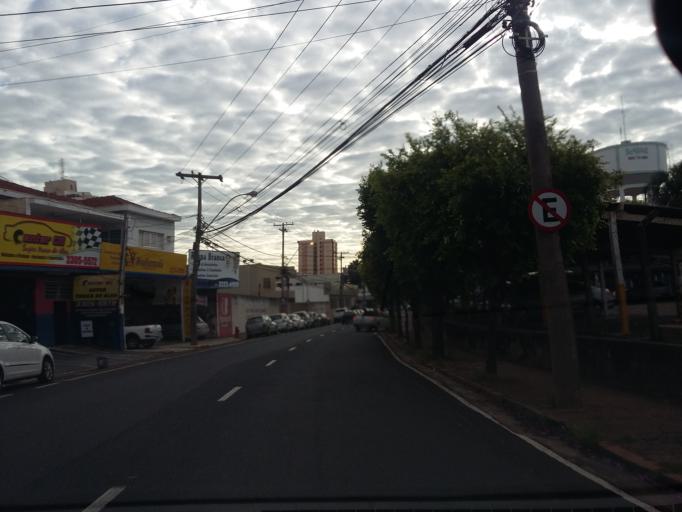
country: BR
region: Sao Paulo
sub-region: Sao Jose Do Rio Preto
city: Sao Jose do Rio Preto
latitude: -20.8222
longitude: -49.3921
